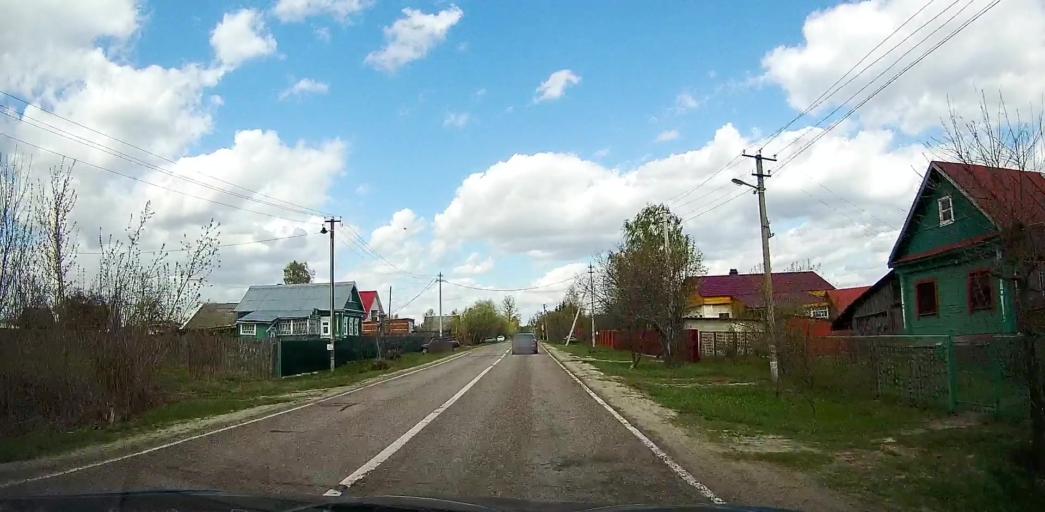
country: RU
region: Moskovskaya
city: Davydovo
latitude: 55.5820
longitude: 38.8256
